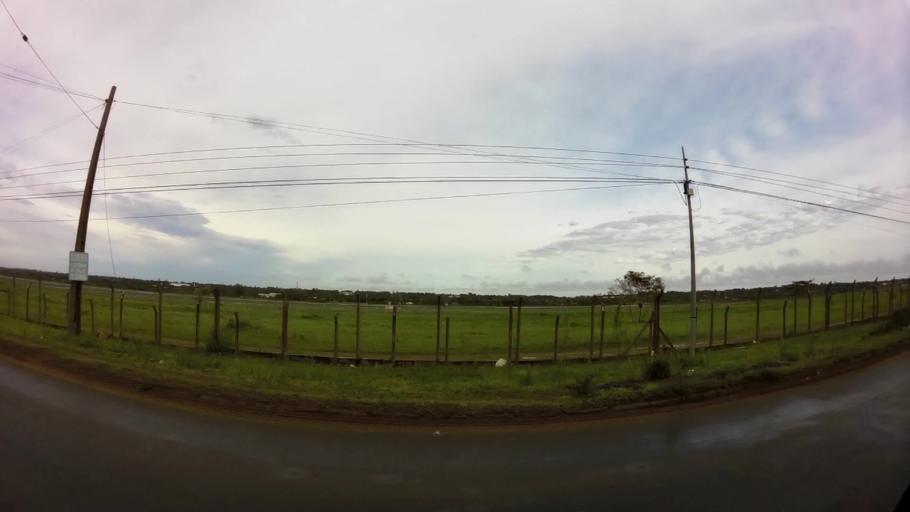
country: PY
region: Central
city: Limpio
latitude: -25.2285
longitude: -57.5113
